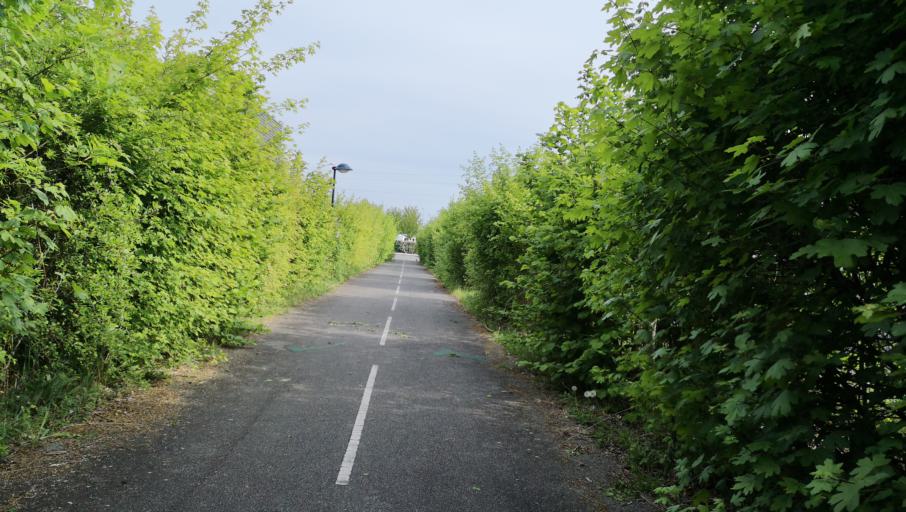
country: FR
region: Centre
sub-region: Departement du Loiret
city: Semoy
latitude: 47.9253
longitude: 1.9455
